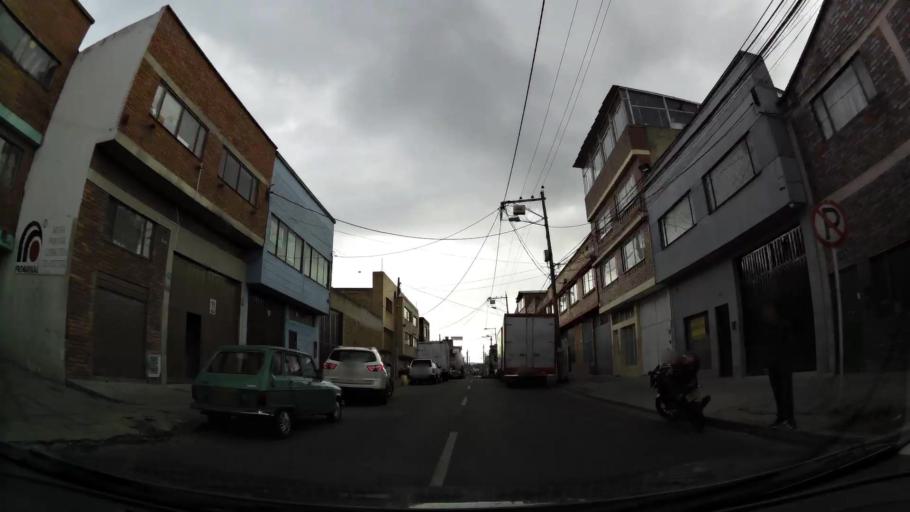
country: CO
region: Bogota D.C.
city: Barrio San Luis
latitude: 4.6718
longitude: -74.0726
